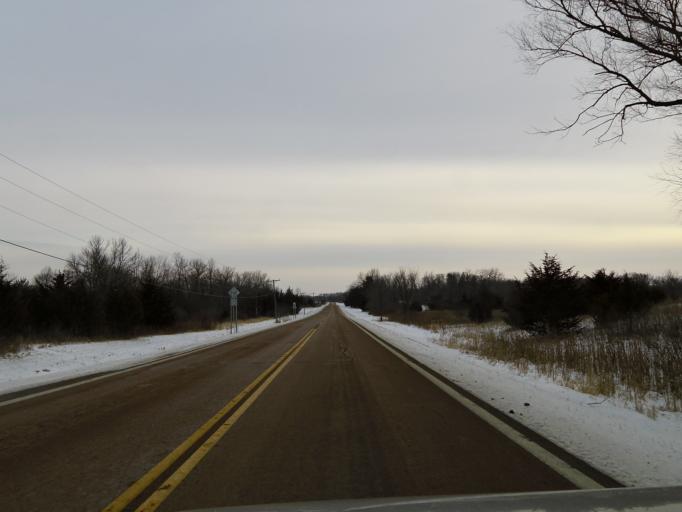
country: US
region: Minnesota
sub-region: Hennepin County
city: Saint Bonifacius
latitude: 44.8880
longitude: -93.7052
